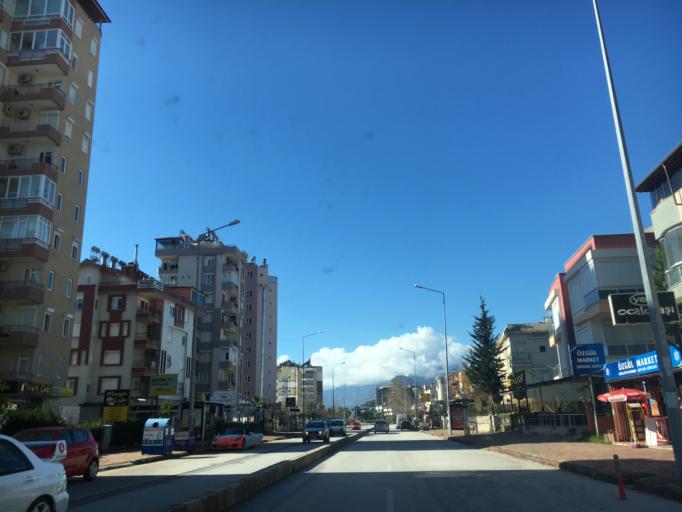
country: TR
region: Antalya
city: Antalya
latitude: 36.8741
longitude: 30.6522
